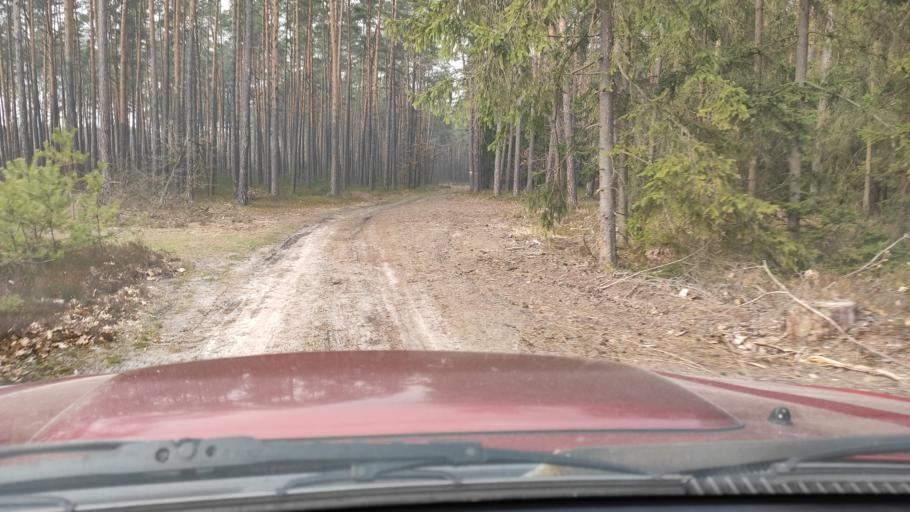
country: PL
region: Masovian Voivodeship
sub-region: Powiat zwolenski
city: Zwolen
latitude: 51.3956
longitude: 21.5711
